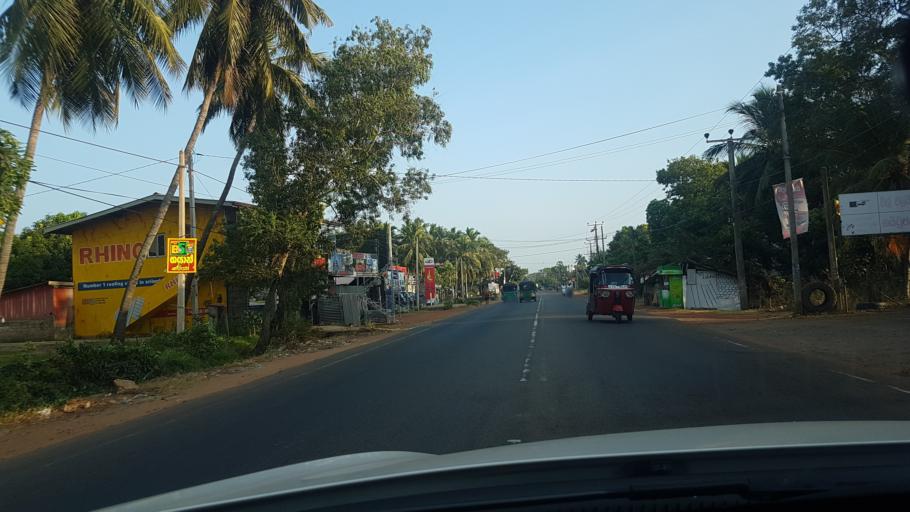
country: LK
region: North Western
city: Chilaw
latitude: 7.5633
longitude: 79.8035
